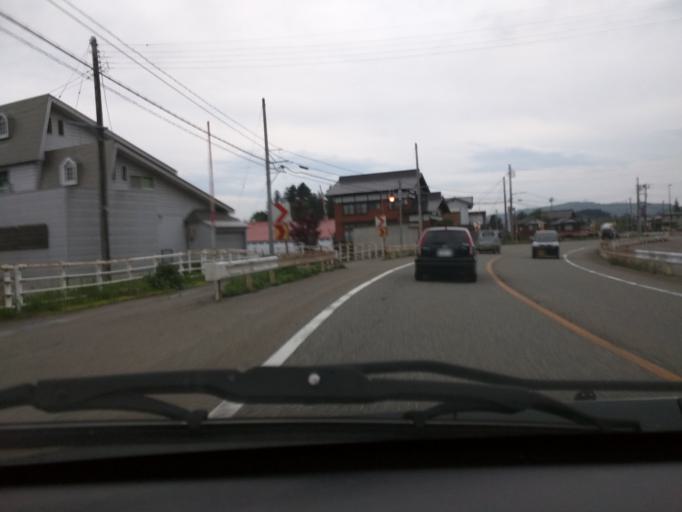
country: JP
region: Niigata
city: Ojiya
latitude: 37.2575
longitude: 138.8715
